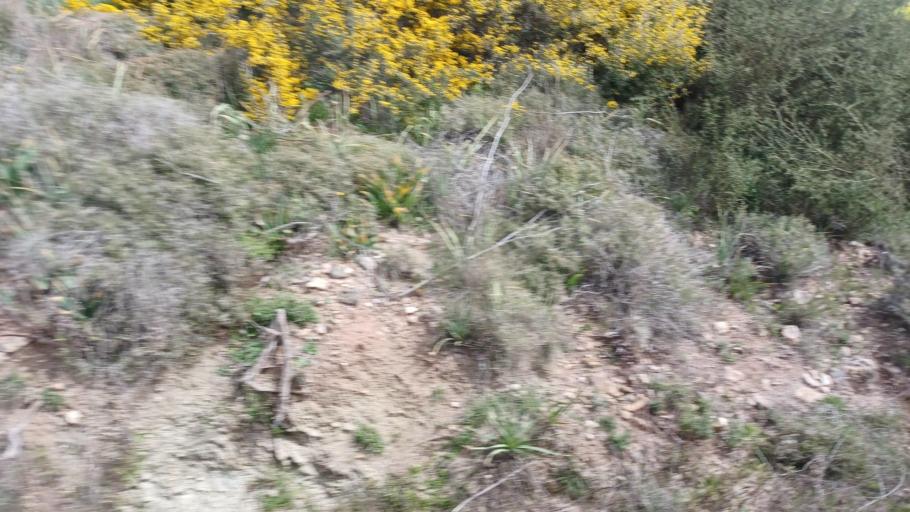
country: CY
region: Pafos
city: Pegeia
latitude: 34.9719
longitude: 32.3585
